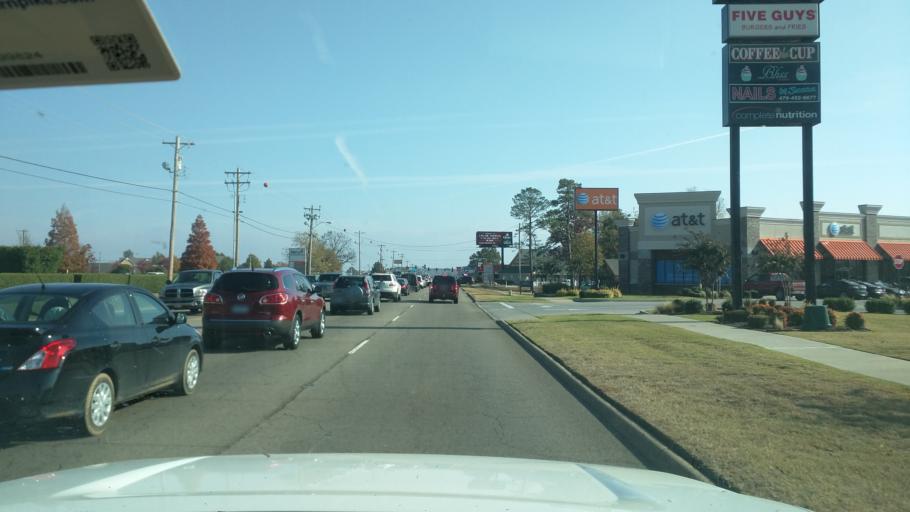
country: US
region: Arkansas
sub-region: Sebastian County
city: Fort Smith
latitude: 35.3541
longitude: -94.3542
